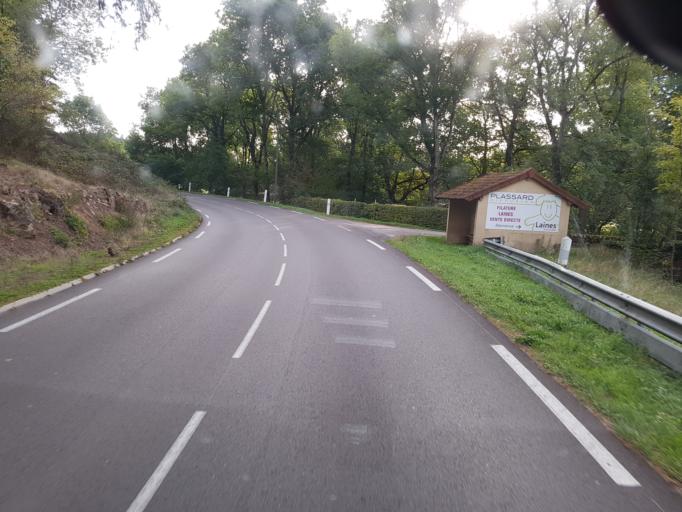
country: FR
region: Bourgogne
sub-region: Departement de Saone-et-Loire
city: La Clayette
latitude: 46.2849
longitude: 4.3418
